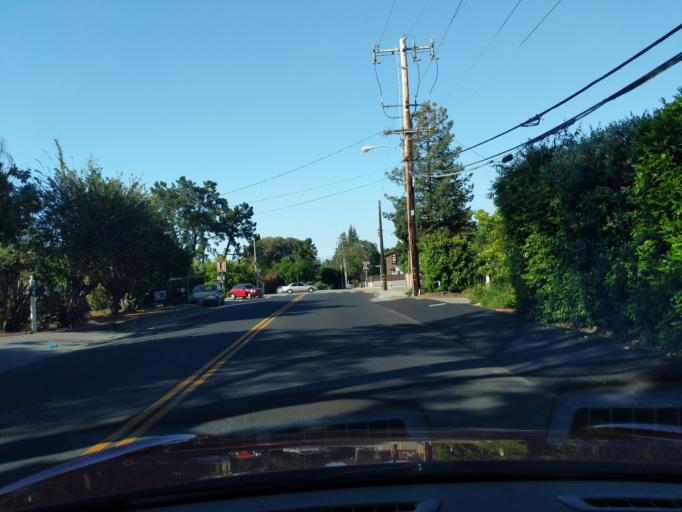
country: US
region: California
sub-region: San Mateo County
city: West Menlo Park
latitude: 37.4299
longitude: -122.1994
